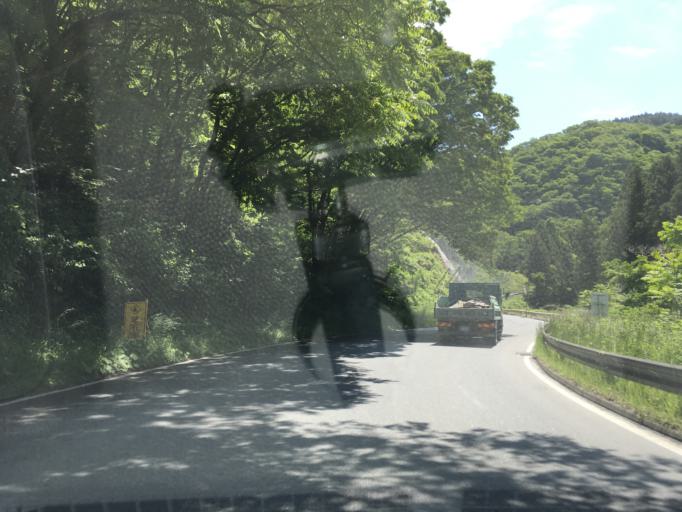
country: JP
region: Miyagi
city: Wakuya
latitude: 38.6576
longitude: 141.3172
